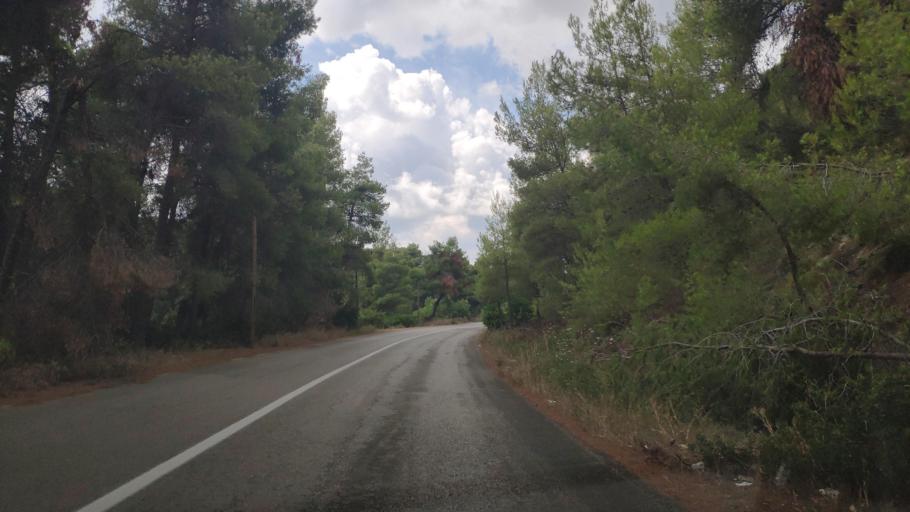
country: GR
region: Central Greece
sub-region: Nomos Fthiotidos
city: Malesina
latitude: 38.6403
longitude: 23.1963
